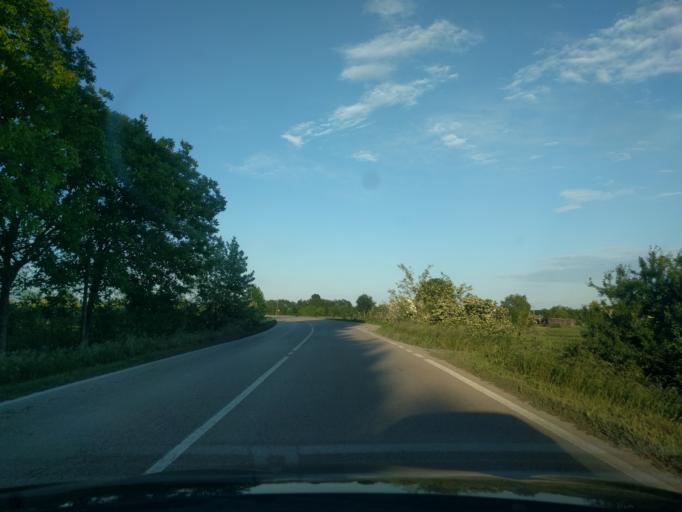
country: IT
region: Veneto
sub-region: Provincia di Rovigo
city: Guarda Veneta
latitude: 44.9827
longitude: 11.8344
